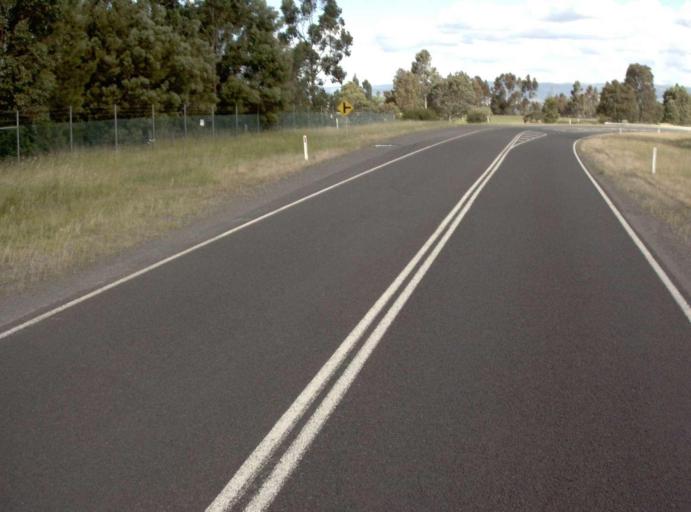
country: AU
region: Victoria
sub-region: Latrobe
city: Moe
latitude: -38.1874
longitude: 146.3290
